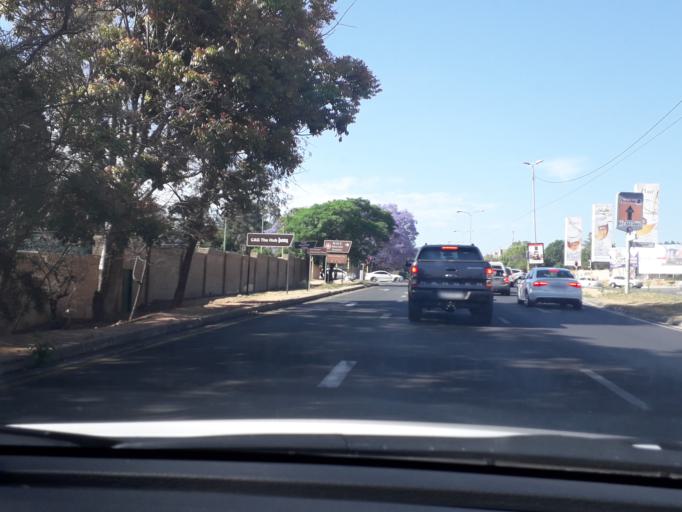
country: ZA
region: Gauteng
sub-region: City of Johannesburg Metropolitan Municipality
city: Diepsloot
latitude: -26.0463
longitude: 28.0250
